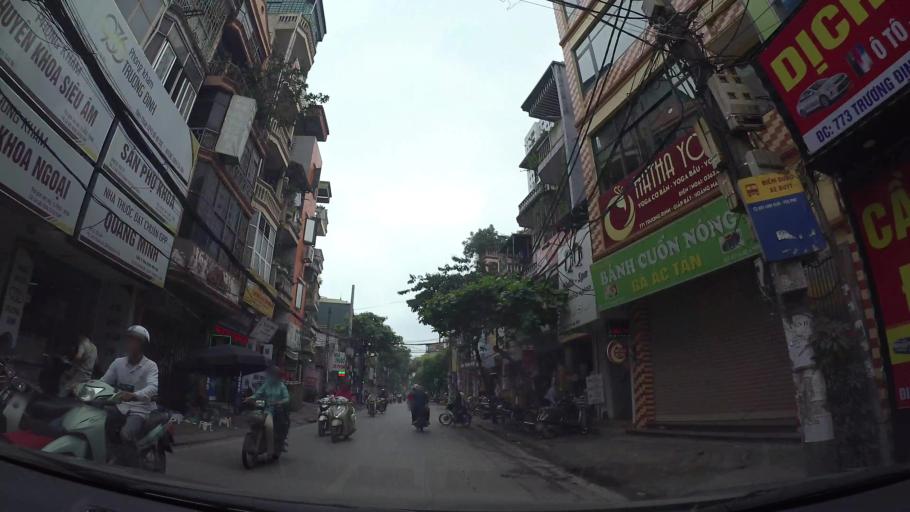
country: VN
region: Ha Noi
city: Van Dien
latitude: 20.9772
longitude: 105.8416
